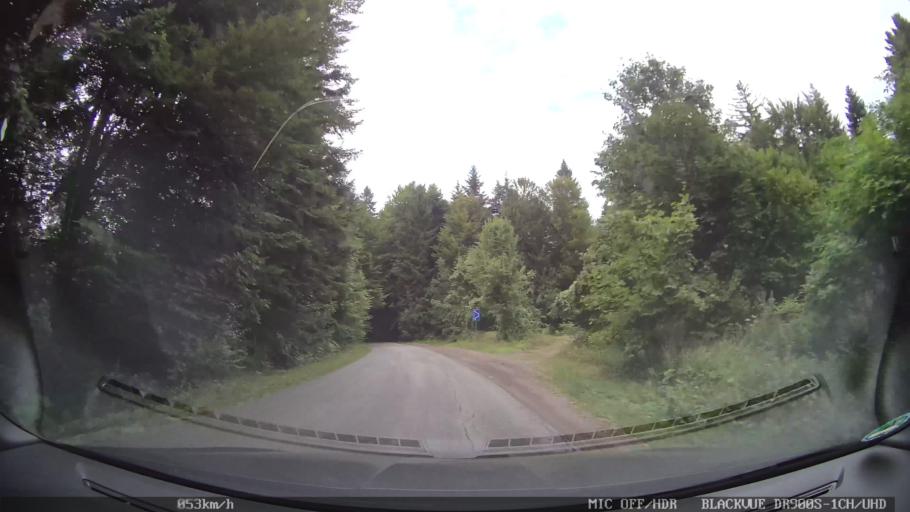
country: HR
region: Licko-Senjska
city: Jezerce
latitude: 44.9317
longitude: 15.5527
